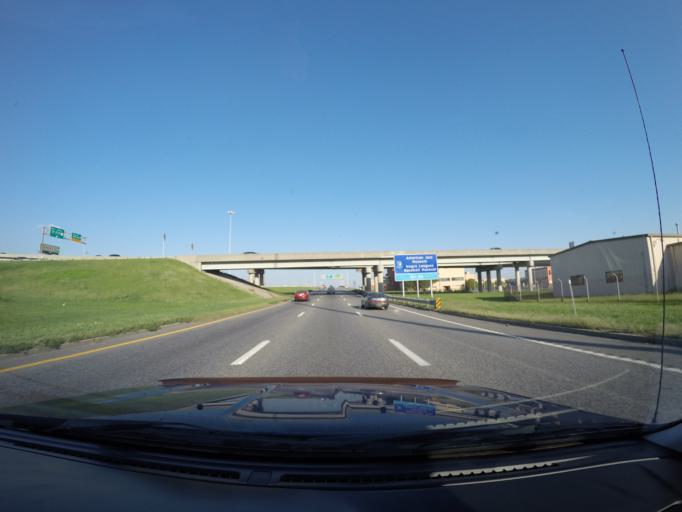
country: US
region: Missouri
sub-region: Jackson County
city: Kansas City
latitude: 39.0962
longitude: -94.5723
